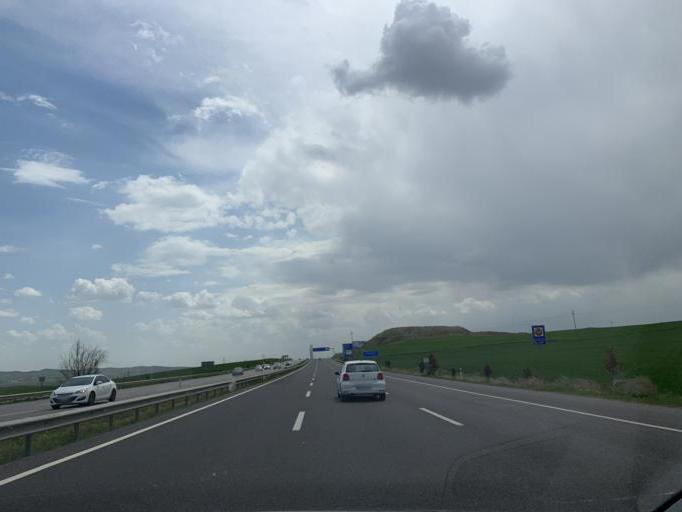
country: TR
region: Ankara
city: Polatli
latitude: 39.5975
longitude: 32.1758
